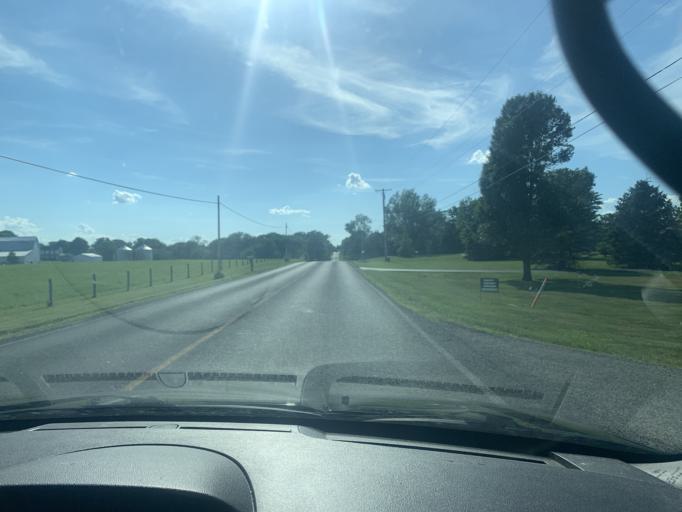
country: US
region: Ohio
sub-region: Logan County
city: Bellefontaine
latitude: 40.3481
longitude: -83.7849
